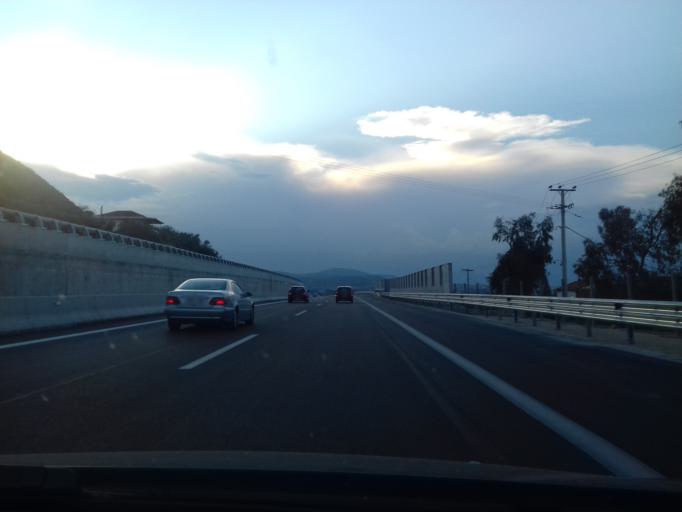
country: GR
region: West Greece
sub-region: Nomos Achaias
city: Temeni
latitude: 38.2123
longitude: 22.1243
